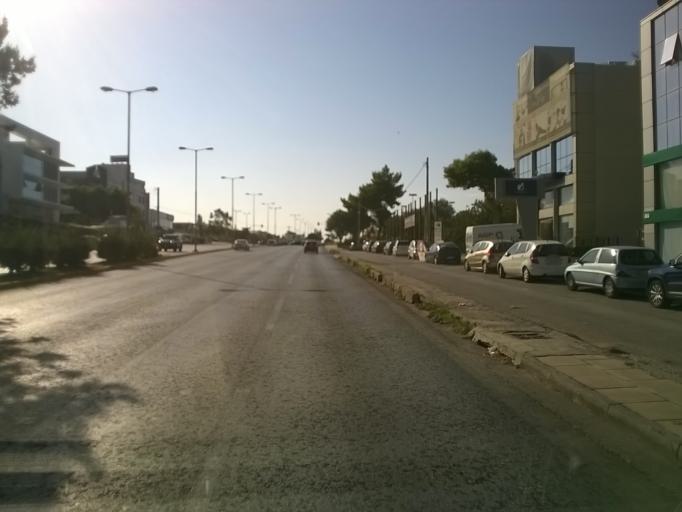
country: GR
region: Attica
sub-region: Nomarchia Athinas
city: Glyfada
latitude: 37.8552
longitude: 23.7661
